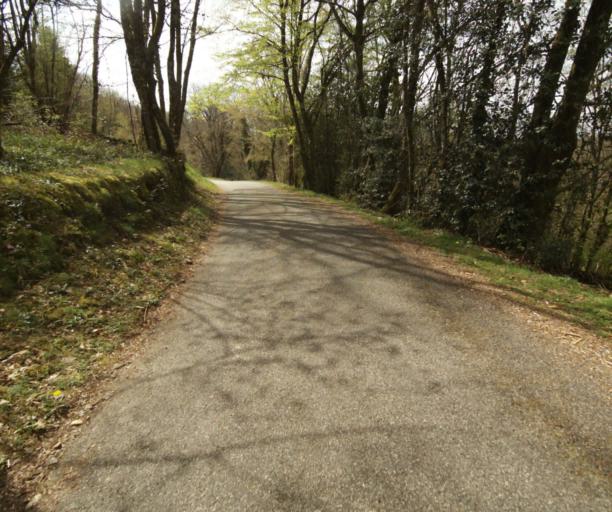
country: FR
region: Limousin
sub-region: Departement de la Correze
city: Laguenne
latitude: 45.1982
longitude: 1.8823
